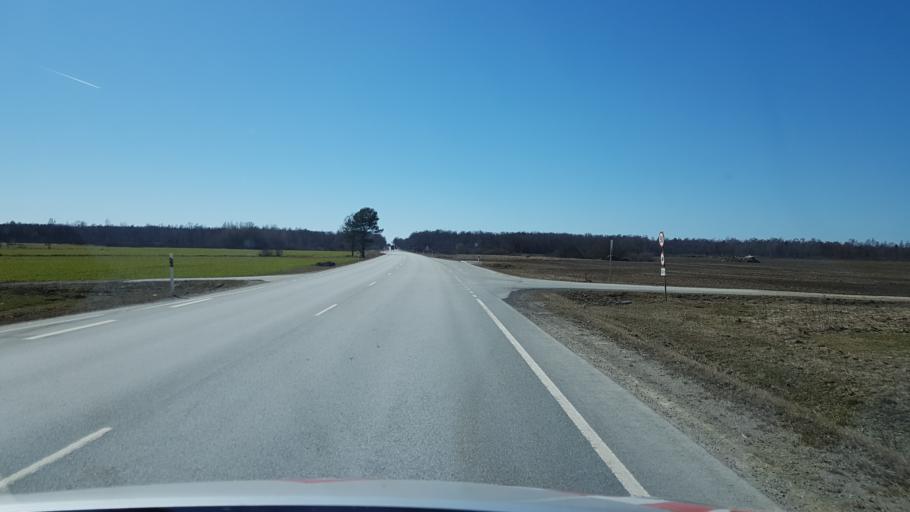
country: EE
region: Laeaene-Virumaa
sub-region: Someru vald
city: Someru
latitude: 59.4506
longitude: 26.4184
